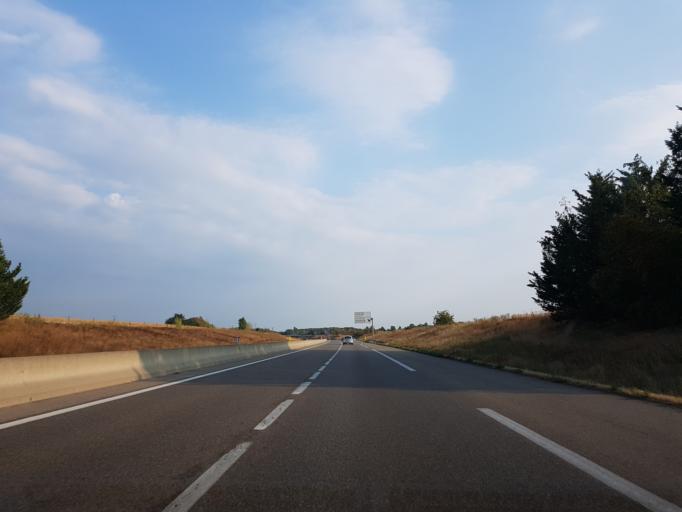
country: FR
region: Alsace
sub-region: Departement du Haut-Rhin
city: Baldersheim
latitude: 47.8011
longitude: 7.3930
